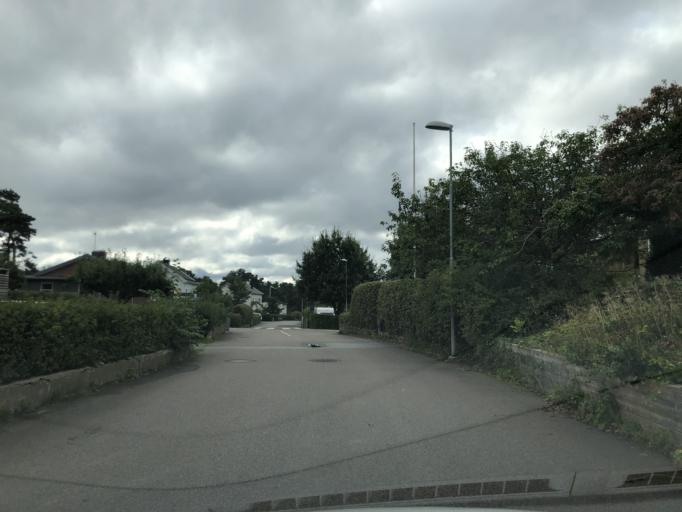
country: SE
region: Vaestra Goetaland
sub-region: Goteborg
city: Majorna
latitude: 57.7416
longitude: 11.9110
